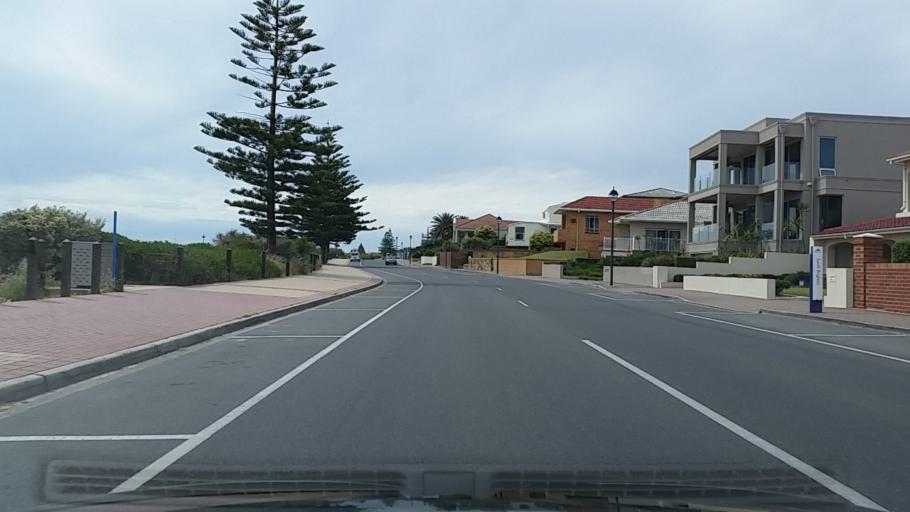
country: AU
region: South Australia
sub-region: Adelaide Hills
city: Seacliff
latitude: -35.0271
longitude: 138.5175
